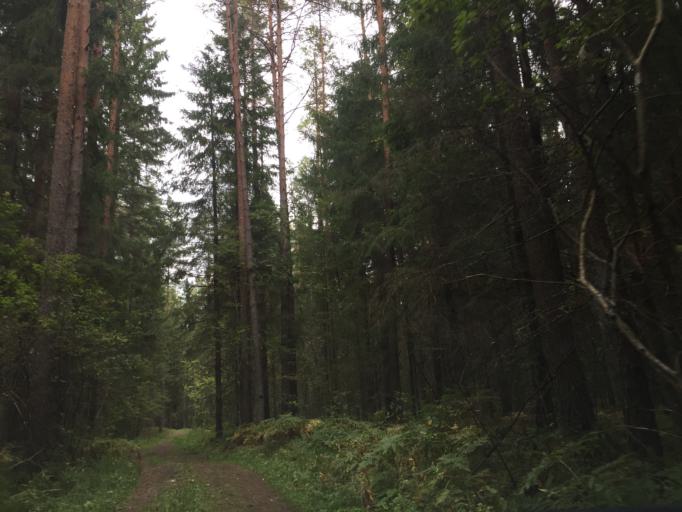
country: LV
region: Baldone
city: Baldone
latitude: 56.7800
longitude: 24.4439
